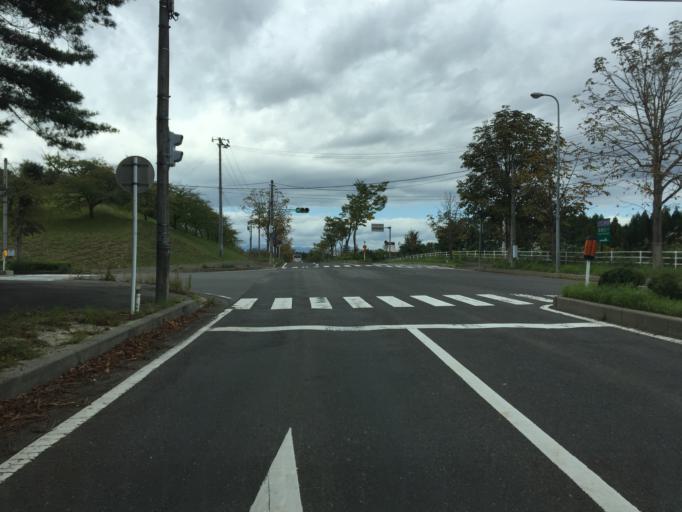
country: JP
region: Fukushima
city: Fukushima-shi
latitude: 37.6885
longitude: 140.4757
